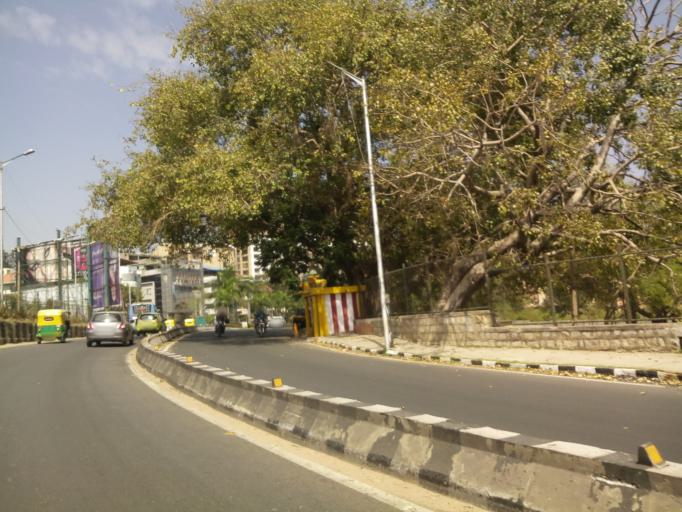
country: IN
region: Karnataka
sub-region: Bangalore Urban
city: Bangalore
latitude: 12.9808
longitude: 77.6222
